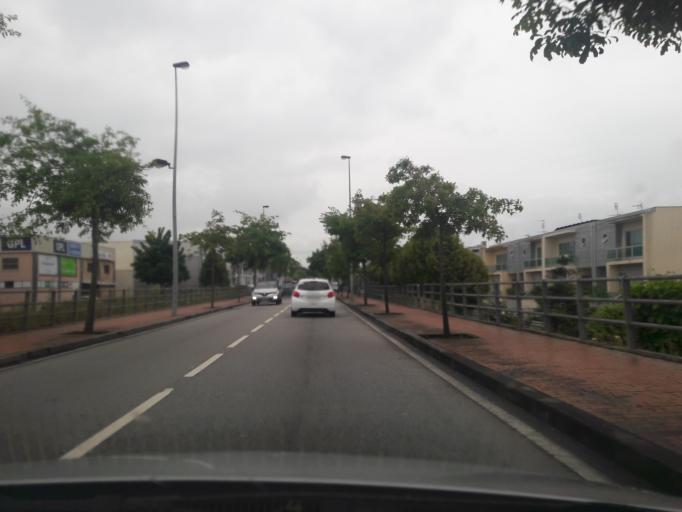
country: PT
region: Porto
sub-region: Vila do Conde
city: Arvore
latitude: 41.3322
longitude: -8.7204
